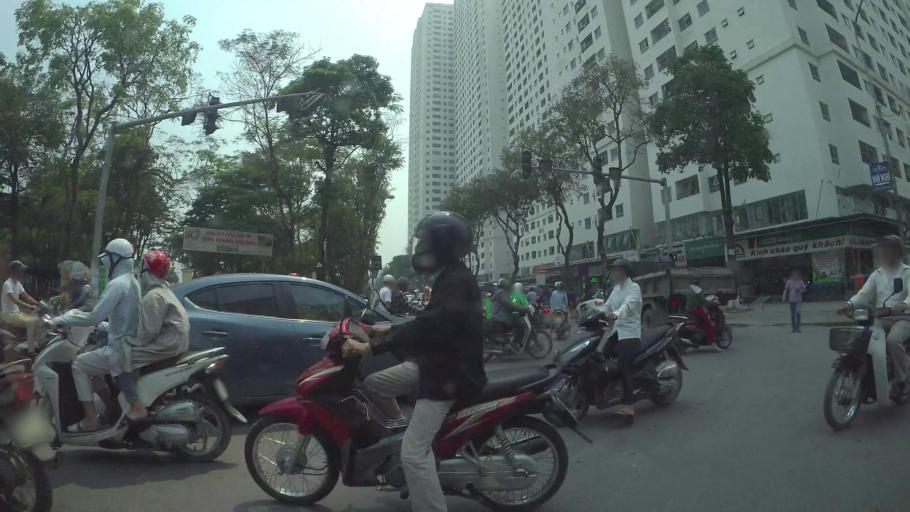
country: VN
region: Ha Noi
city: Van Dien
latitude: 20.9649
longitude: 105.8257
